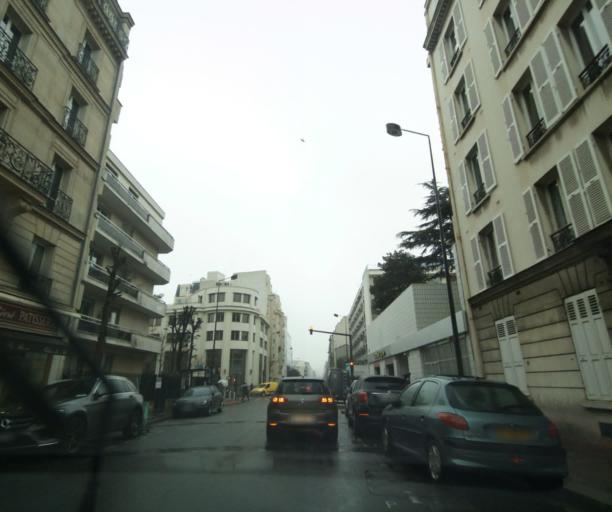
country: FR
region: Ile-de-France
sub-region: Departement des Hauts-de-Seine
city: Levallois-Perret
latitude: 48.8880
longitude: 2.2820
